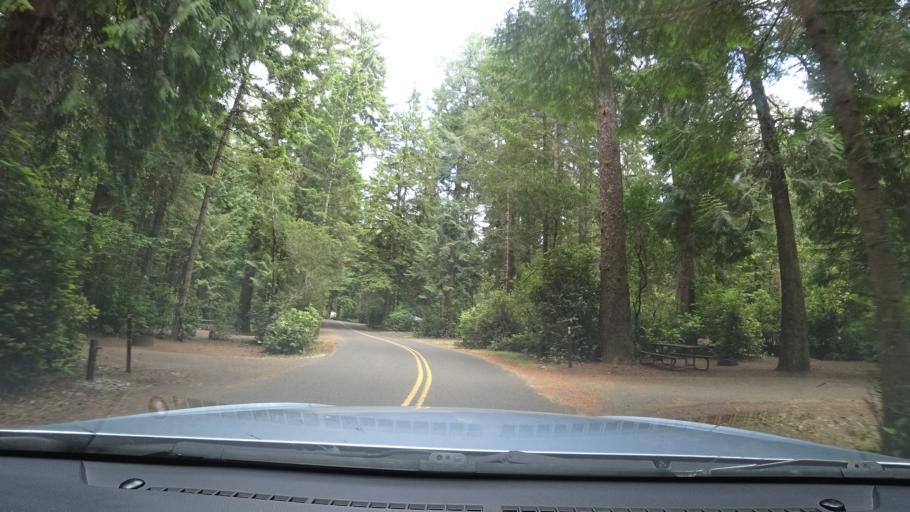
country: US
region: Oregon
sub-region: Lane County
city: Dunes City
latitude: 43.9237
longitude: -124.1117
